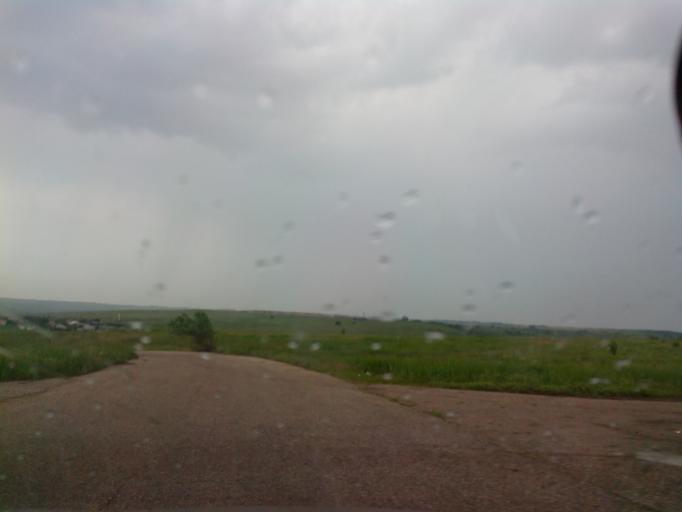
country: RU
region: Volgograd
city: Slashchevskaya
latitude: 49.7817
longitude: 42.4482
